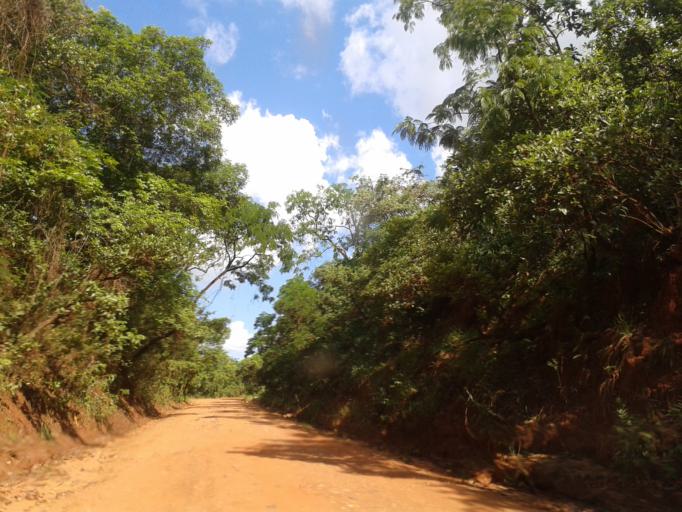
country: BR
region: Minas Gerais
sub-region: Campina Verde
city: Campina Verde
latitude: -19.3183
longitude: -49.8054
